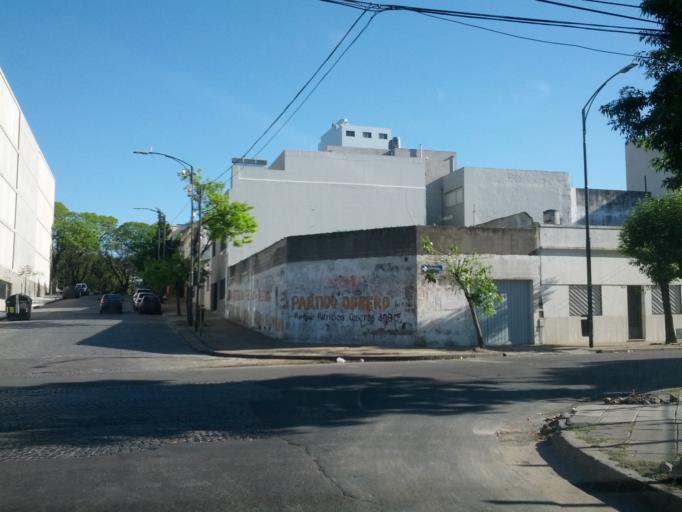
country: AR
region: Buenos Aires F.D.
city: Buenos Aires
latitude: -34.6414
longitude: -58.4063
